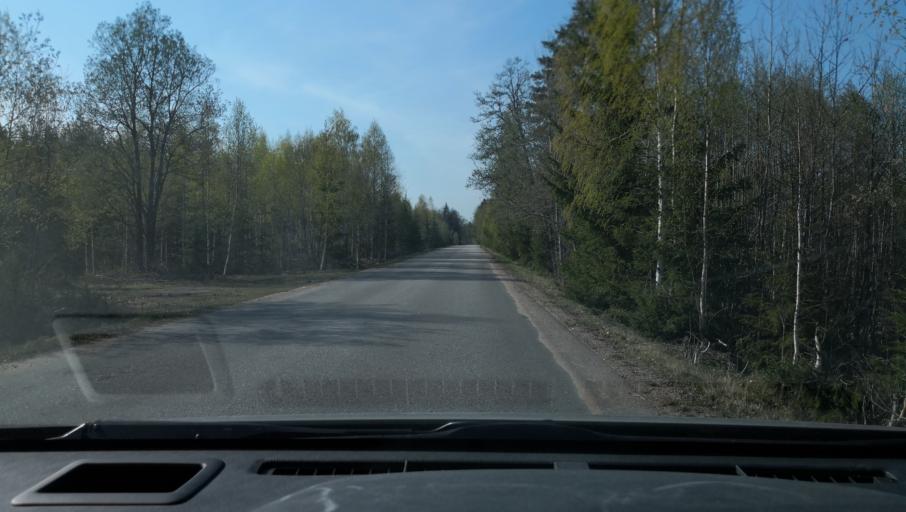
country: SE
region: Uppsala
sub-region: Heby Kommun
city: Tarnsjo
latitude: 60.2622
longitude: 16.9336
